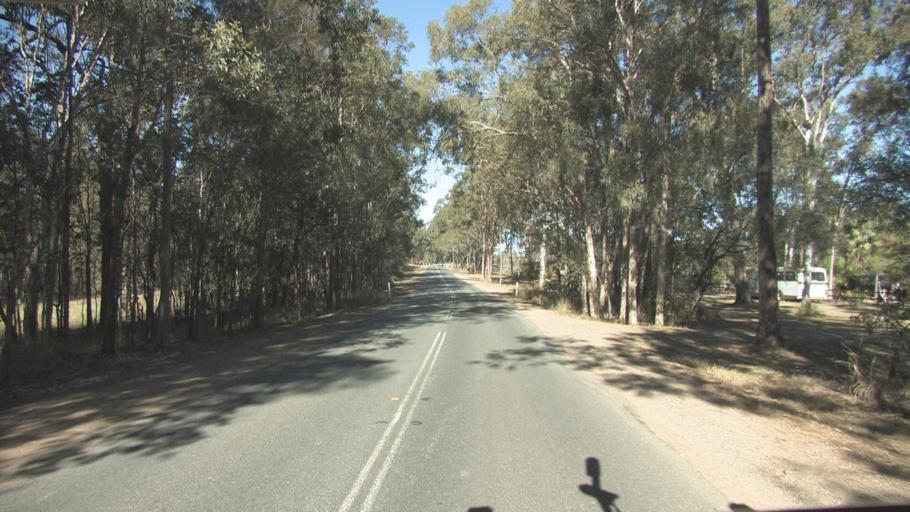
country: AU
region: Queensland
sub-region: Logan
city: North Maclean
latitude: -27.7479
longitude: 152.9915
